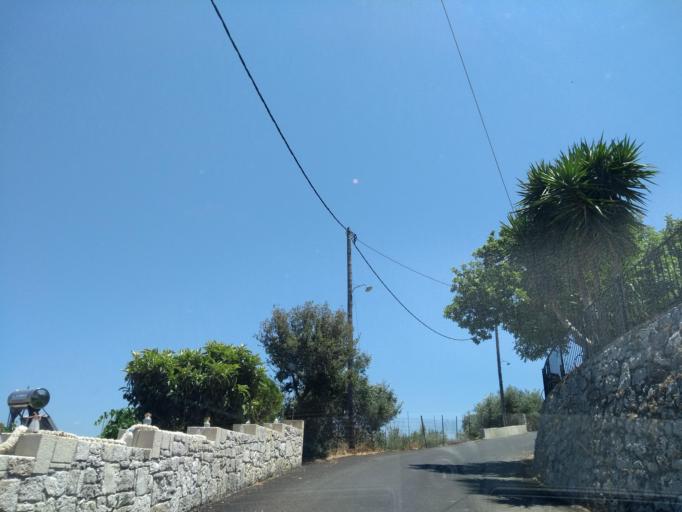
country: GR
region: Crete
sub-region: Nomos Chanias
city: Georgioupolis
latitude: 35.3166
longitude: 24.3091
